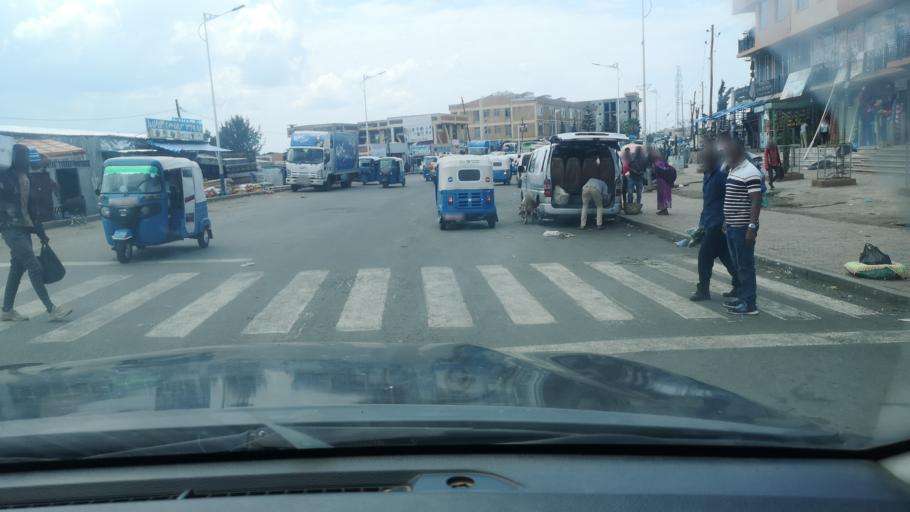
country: ET
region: Oromiya
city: Waliso
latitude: 8.2826
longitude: 37.7794
